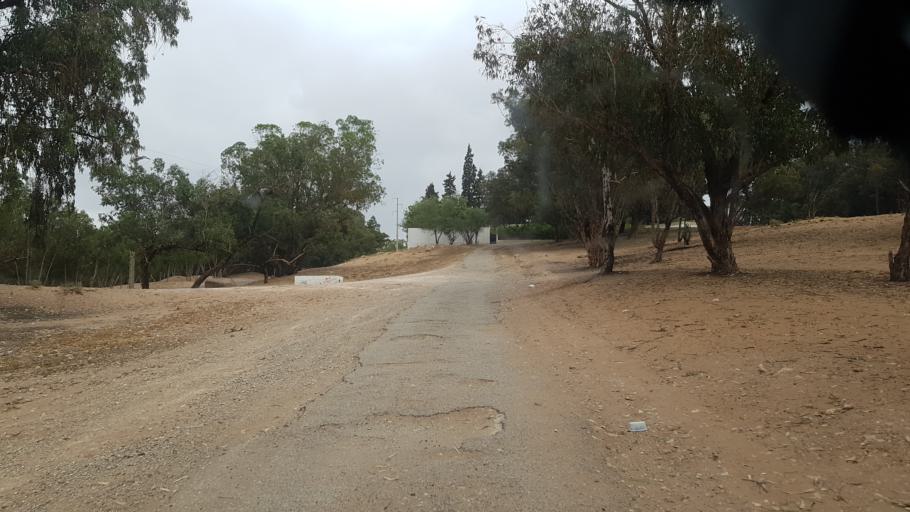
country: MA
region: Souss-Massa-Draa
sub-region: Inezgane-Ait Mellou
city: Inezgane
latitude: 30.3185
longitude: -9.5369
